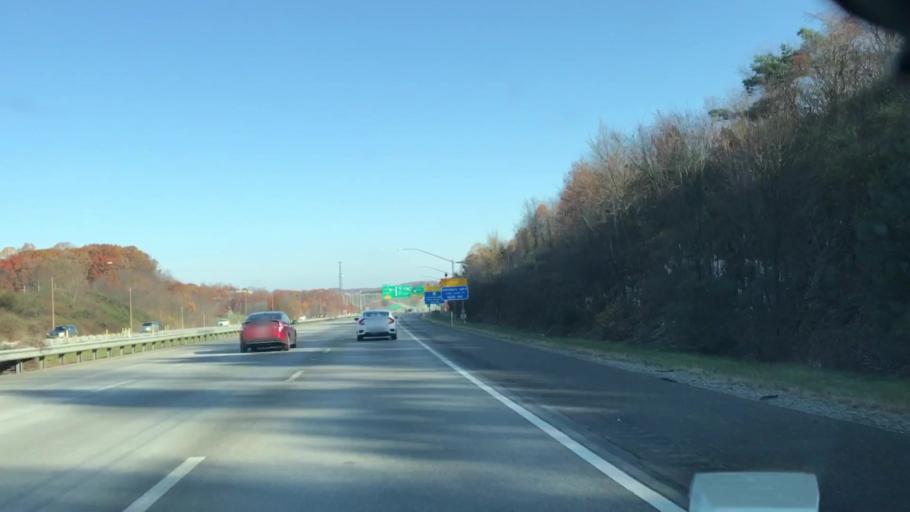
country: US
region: Pennsylvania
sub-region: Allegheny County
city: Bradford Woods
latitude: 40.6423
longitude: -80.0970
